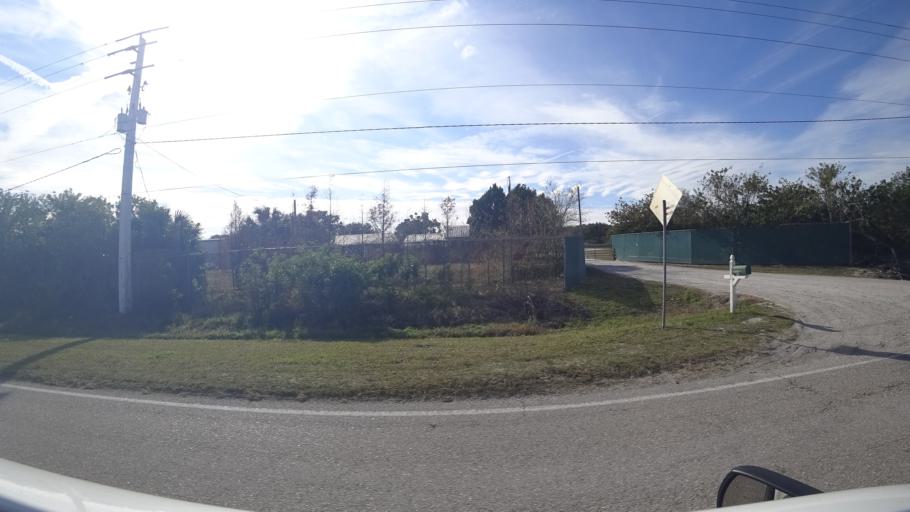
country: US
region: Florida
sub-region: Manatee County
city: Ellenton
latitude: 27.6012
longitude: -82.4696
